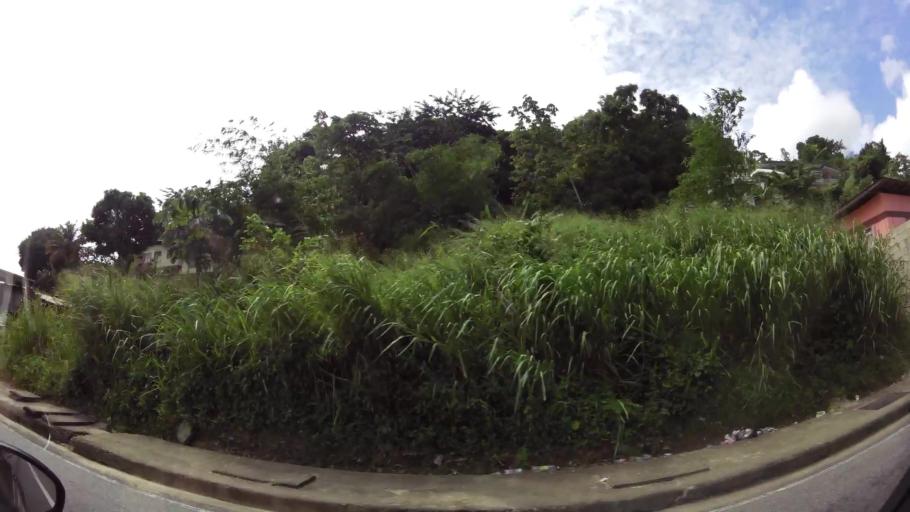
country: TT
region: Diego Martin
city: Petit Valley
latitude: 10.7063
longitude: -61.5565
